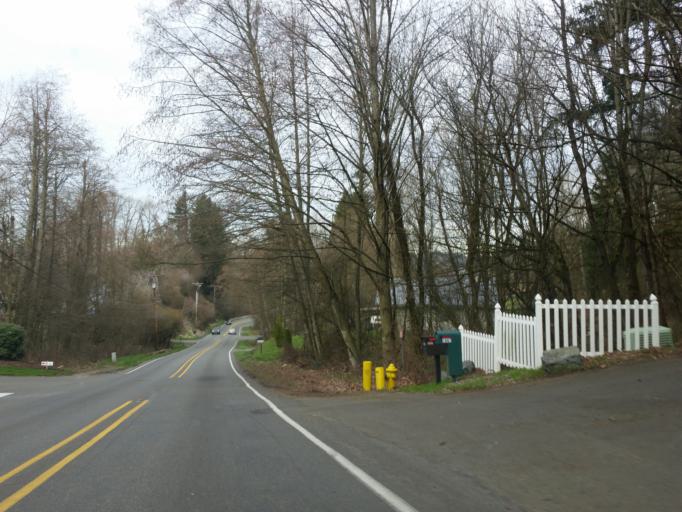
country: US
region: Washington
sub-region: Pierce County
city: Alderton
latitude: 47.1758
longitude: -122.2547
